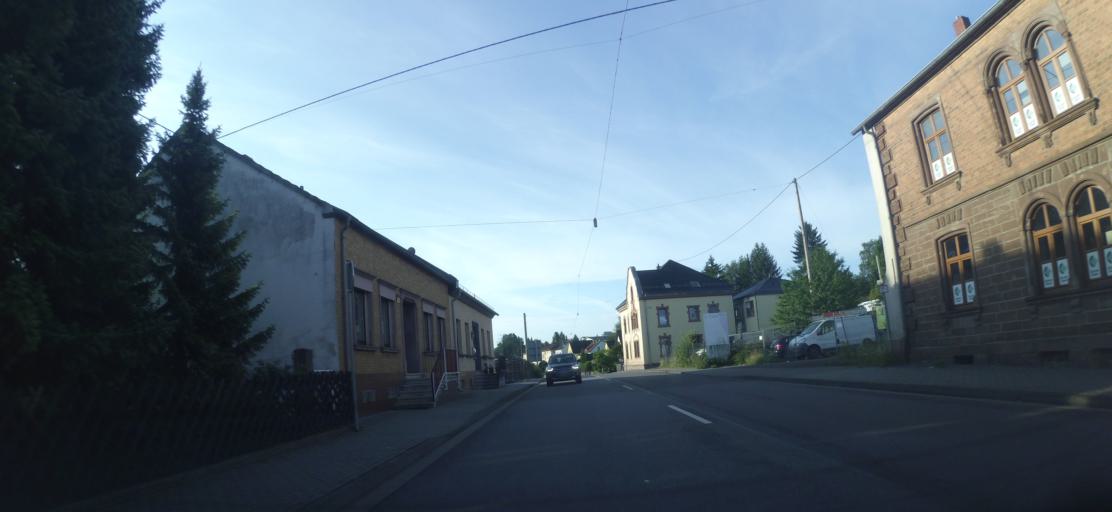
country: DE
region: Saarland
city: Lebach
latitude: 49.4053
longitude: 6.9133
